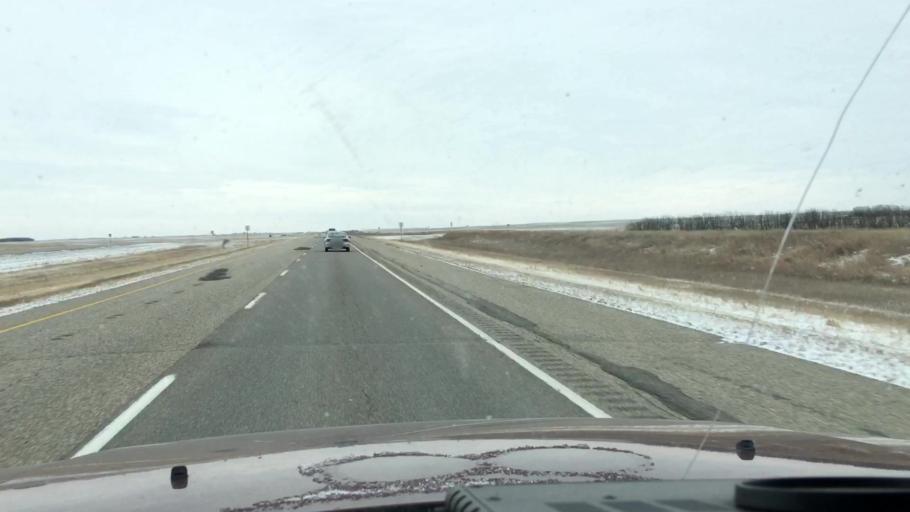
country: CA
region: Saskatchewan
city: Saskatoon
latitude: 51.4653
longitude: -106.2402
